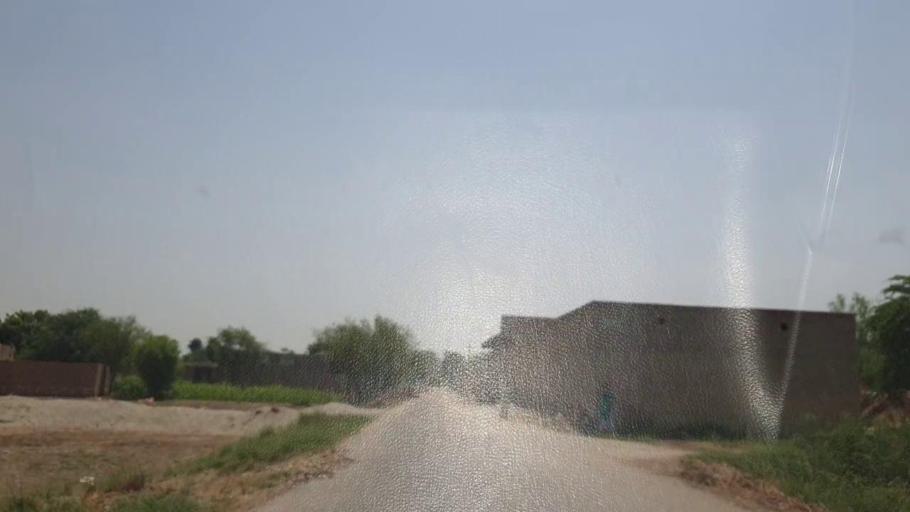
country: PK
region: Sindh
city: Kot Diji
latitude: 27.2812
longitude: 68.6428
